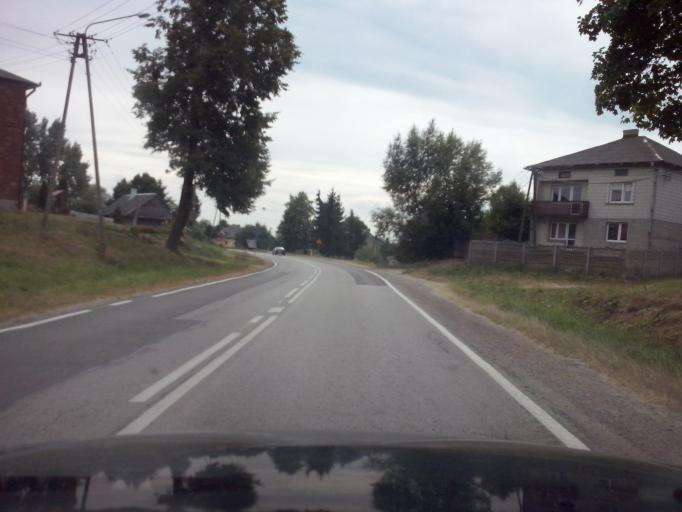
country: PL
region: Swietokrzyskie
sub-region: Powiat kielecki
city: Lagow
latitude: 50.7378
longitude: 21.0733
